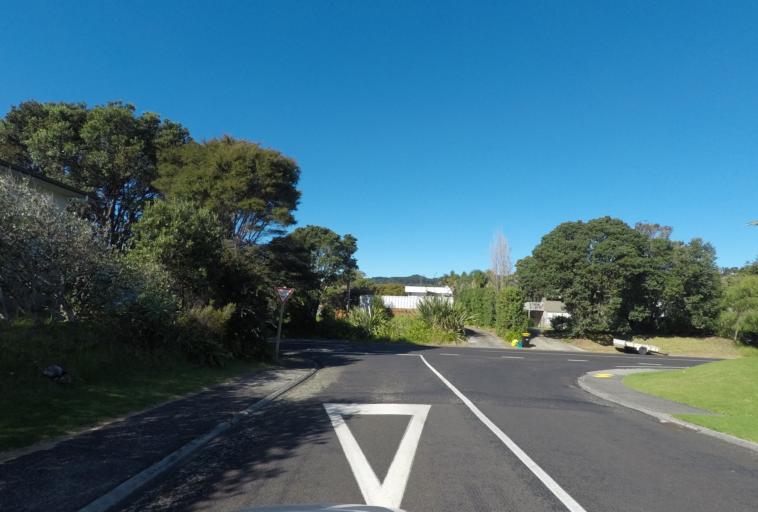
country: NZ
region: Waikato
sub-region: Thames-Coromandel District
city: Whangamata
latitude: -37.2826
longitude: 175.9008
